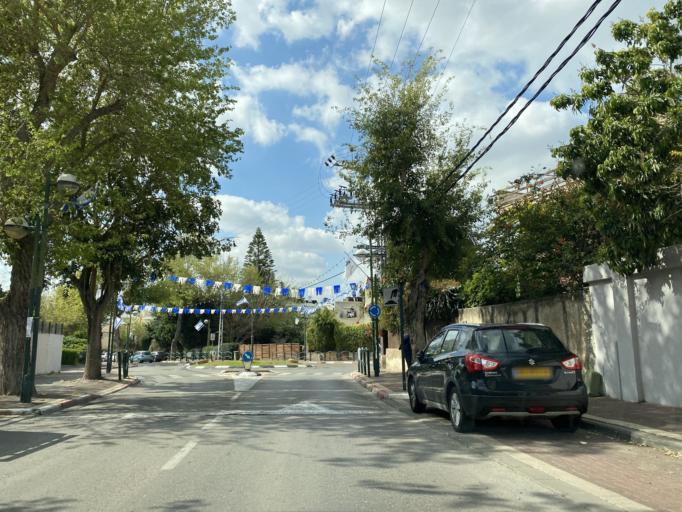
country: IL
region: Tel Aviv
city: Ramat HaSharon
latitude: 32.1346
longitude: 34.8414
